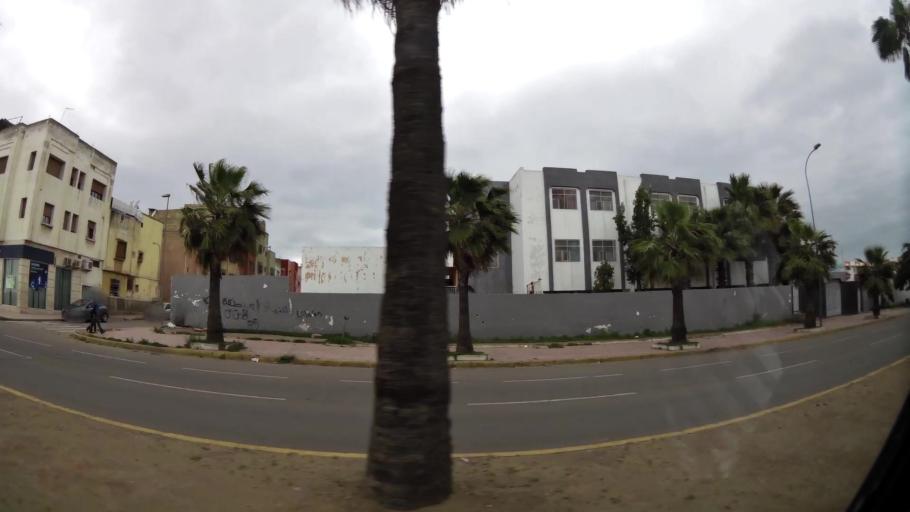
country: MA
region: Grand Casablanca
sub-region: Mediouna
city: Tit Mellil
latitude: 33.5581
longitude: -7.5408
